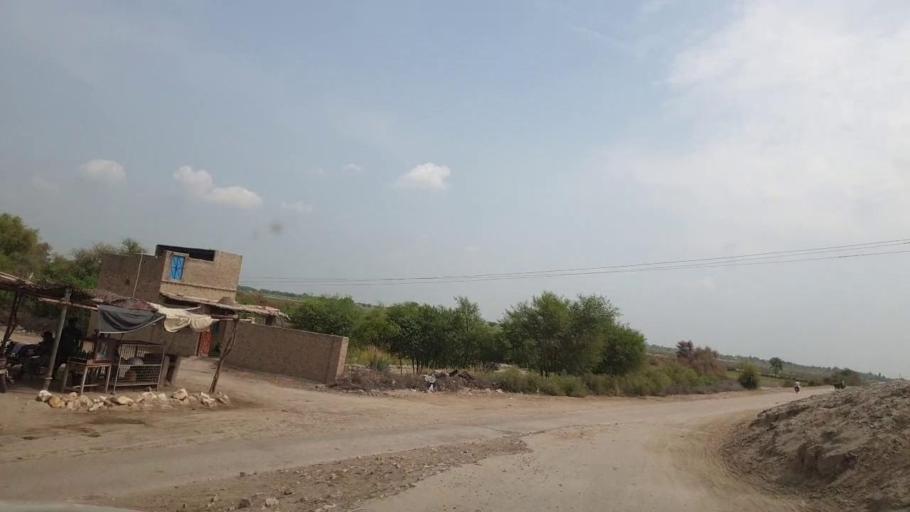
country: PK
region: Sindh
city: Dokri
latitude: 27.4062
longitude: 68.2434
